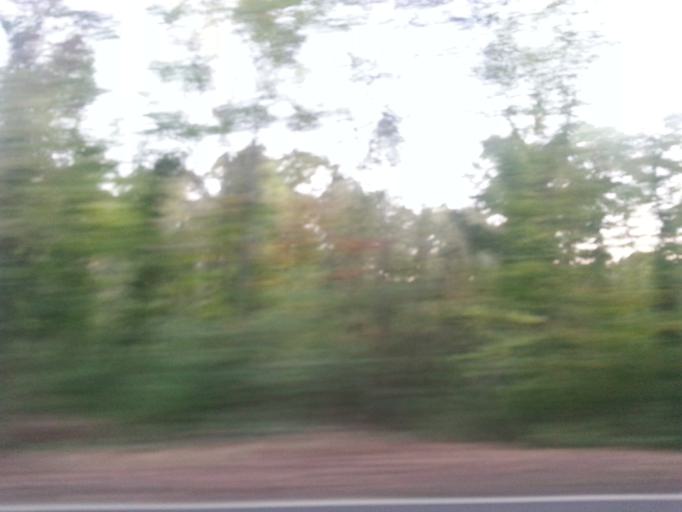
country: US
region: Tennessee
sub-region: Knox County
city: Knoxville
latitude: 36.0182
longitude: -83.9759
